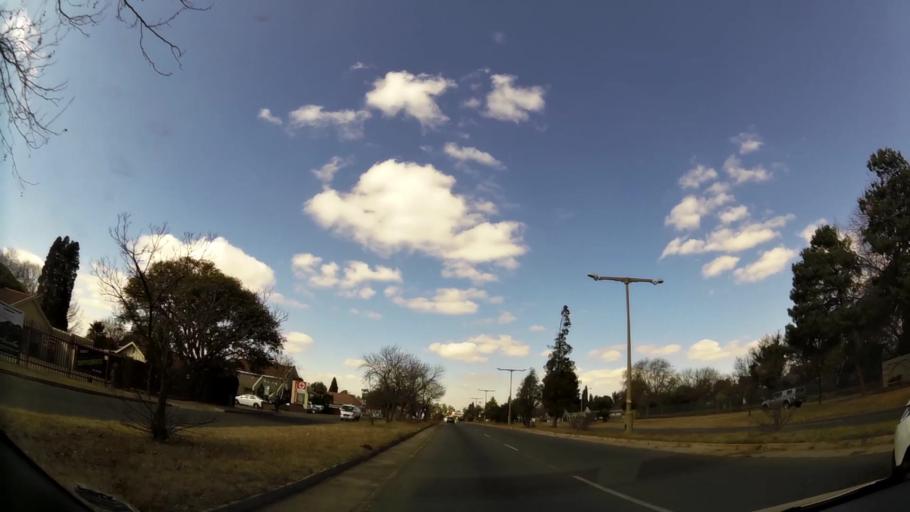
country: ZA
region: Gauteng
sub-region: West Rand District Municipality
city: Krugersdorp
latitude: -26.0966
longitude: 27.7931
